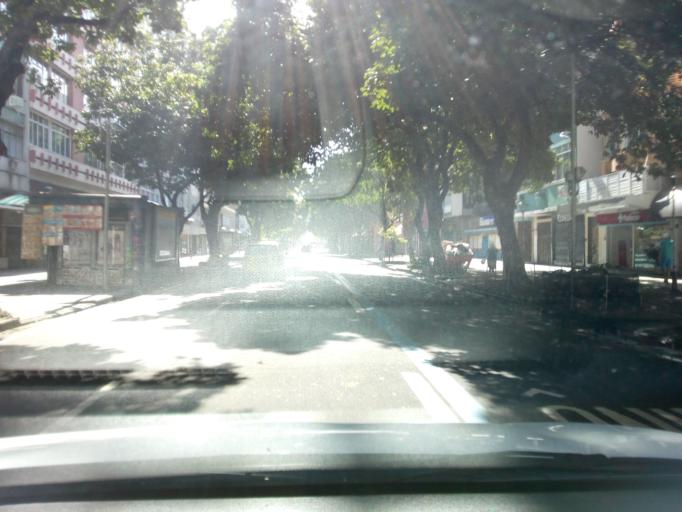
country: BR
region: Rio de Janeiro
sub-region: Rio De Janeiro
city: Rio de Janeiro
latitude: -22.9845
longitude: -43.2006
